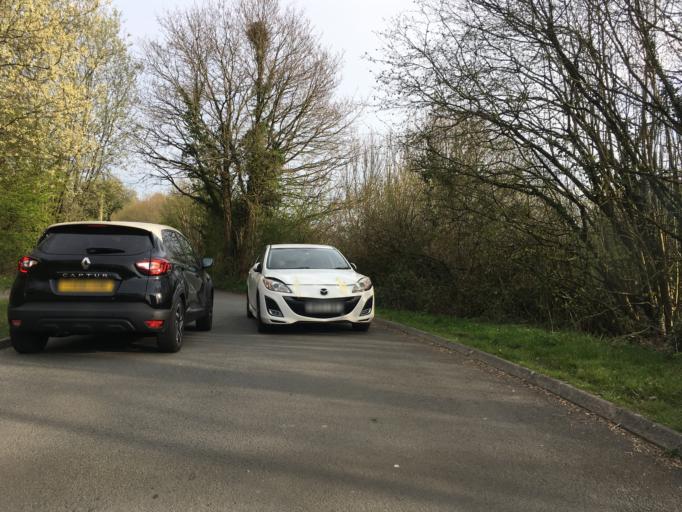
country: GB
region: Wales
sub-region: Caerphilly County Borough
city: Maesycwmmer
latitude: 51.6321
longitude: -3.2295
